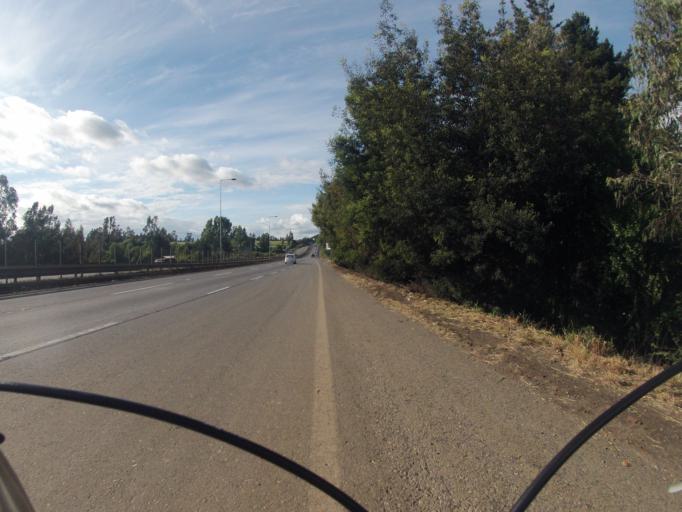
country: CL
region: Araucania
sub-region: Provincia de Cautin
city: Temuco
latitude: -38.8182
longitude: -72.6236
